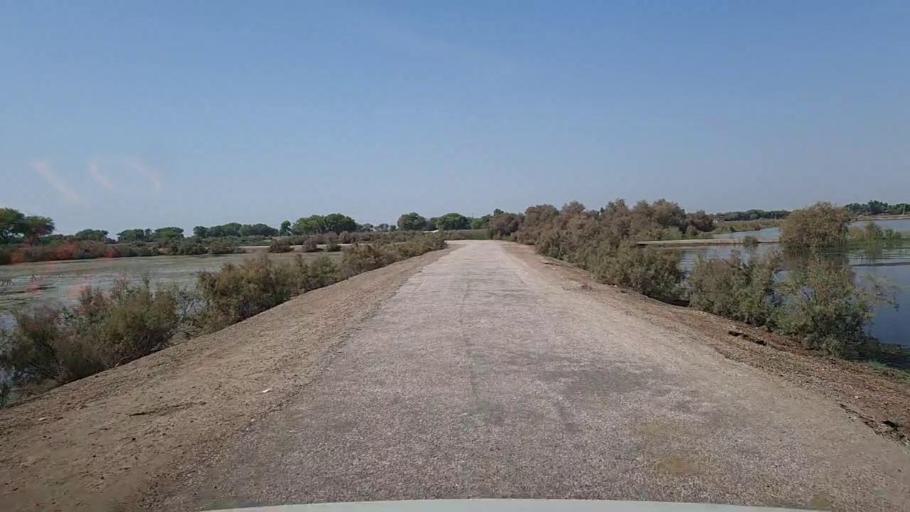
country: PK
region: Sindh
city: Kandhkot
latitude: 28.3372
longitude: 69.3641
